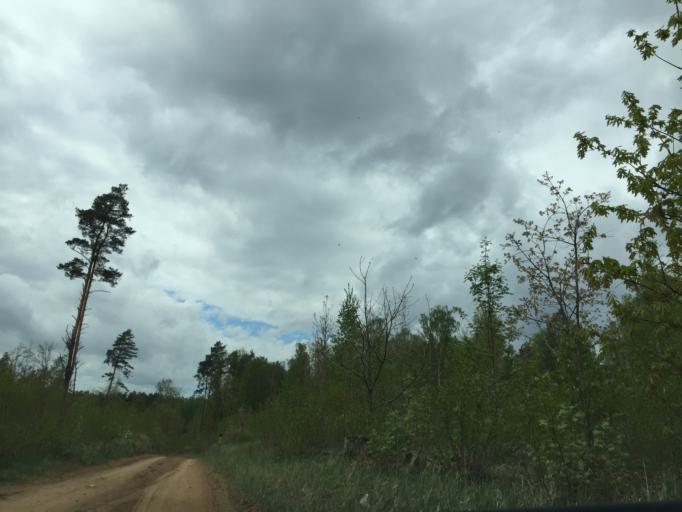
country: LV
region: Kekava
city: Kekava
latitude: 56.8005
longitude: 24.3020
